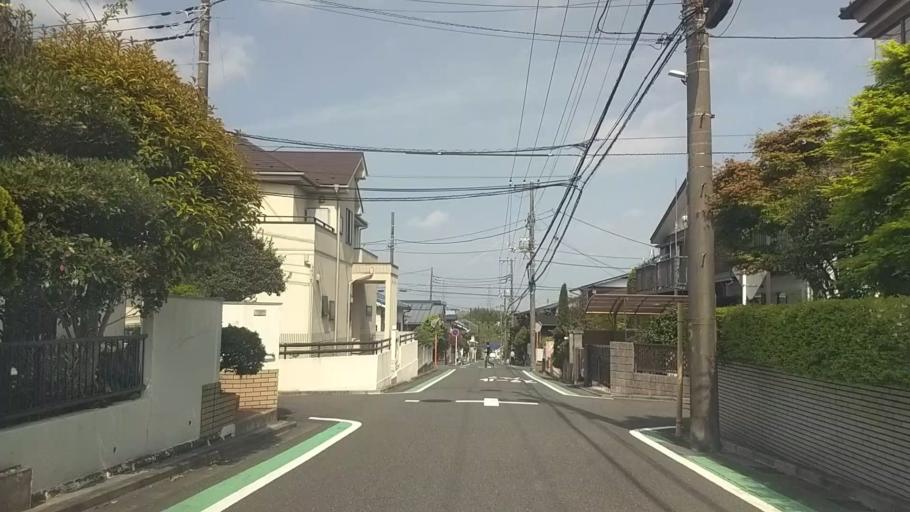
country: JP
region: Kanagawa
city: Yokohama
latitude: 35.3722
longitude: 139.6147
